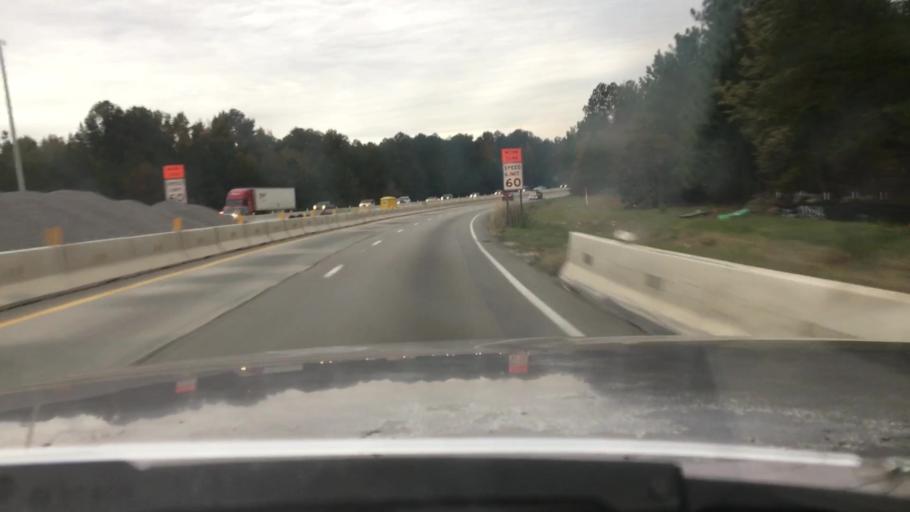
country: US
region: South Carolina
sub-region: Lexington County
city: Lexington
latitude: 33.9707
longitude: -81.1986
